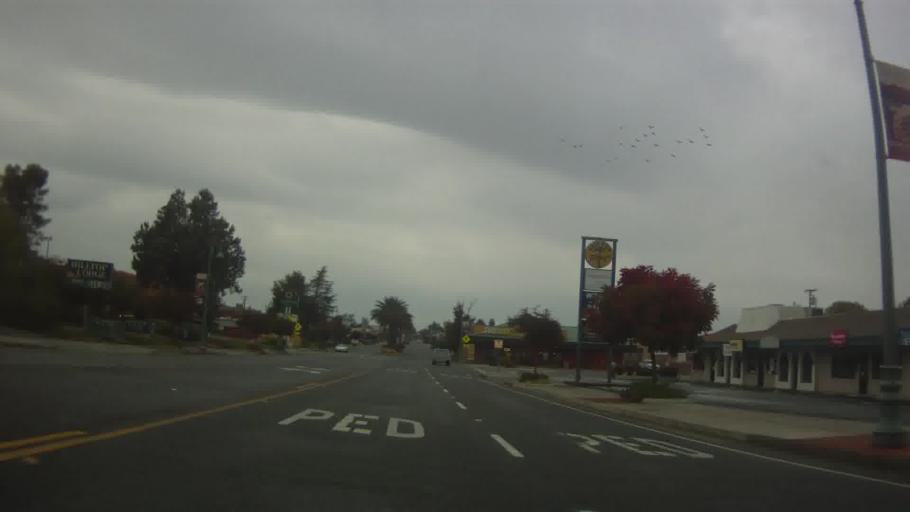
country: US
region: California
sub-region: Shasta County
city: Redding
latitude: 40.5748
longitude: -122.3579
